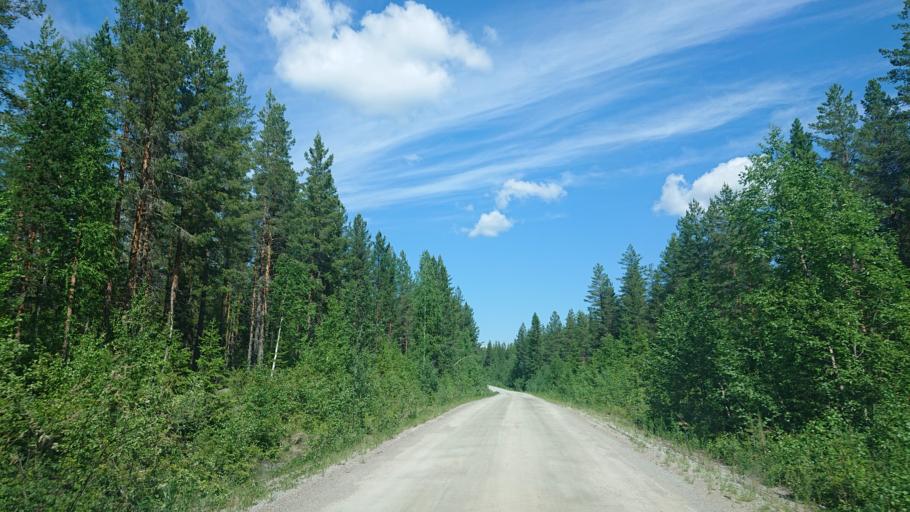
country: SE
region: Vaesternorrland
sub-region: Solleftea Kommun
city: Solleftea
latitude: 62.9499
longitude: 17.1384
